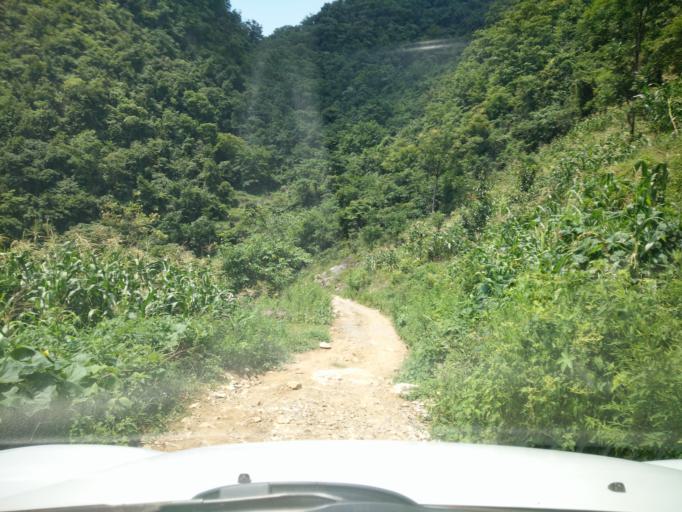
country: CN
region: Guangxi Zhuangzu Zizhiqu
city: Xinzhou
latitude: 25.0148
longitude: 105.7037
